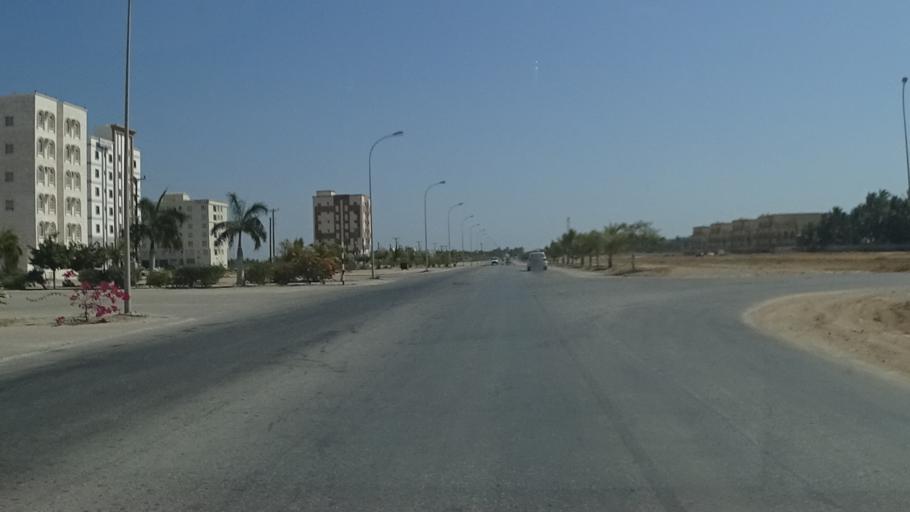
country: OM
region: Zufar
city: Salalah
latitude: 17.0478
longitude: 54.1685
